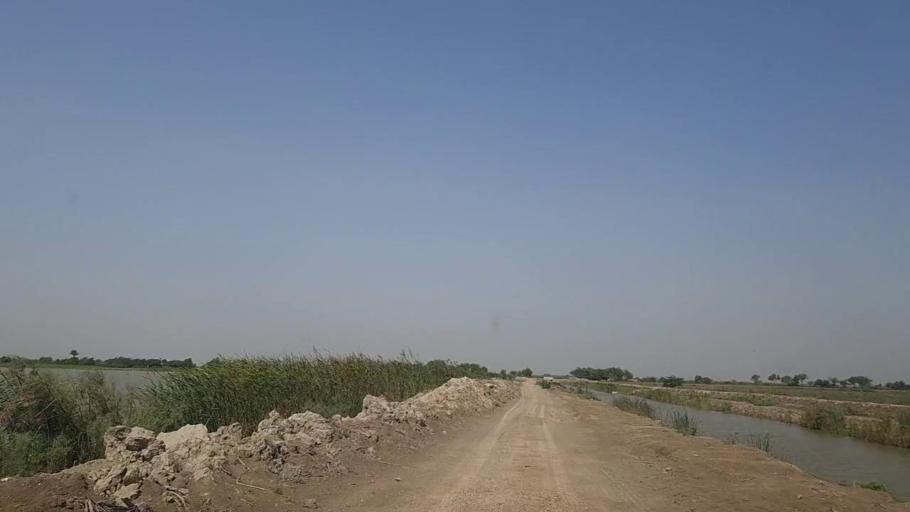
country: PK
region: Sindh
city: Daro Mehar
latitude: 24.7742
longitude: 68.1334
